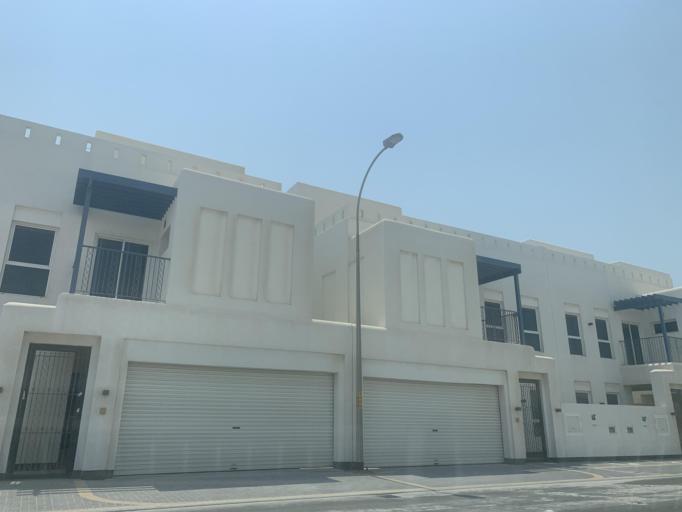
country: BH
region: Muharraq
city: Al Muharraq
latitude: 26.3135
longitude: 50.6243
